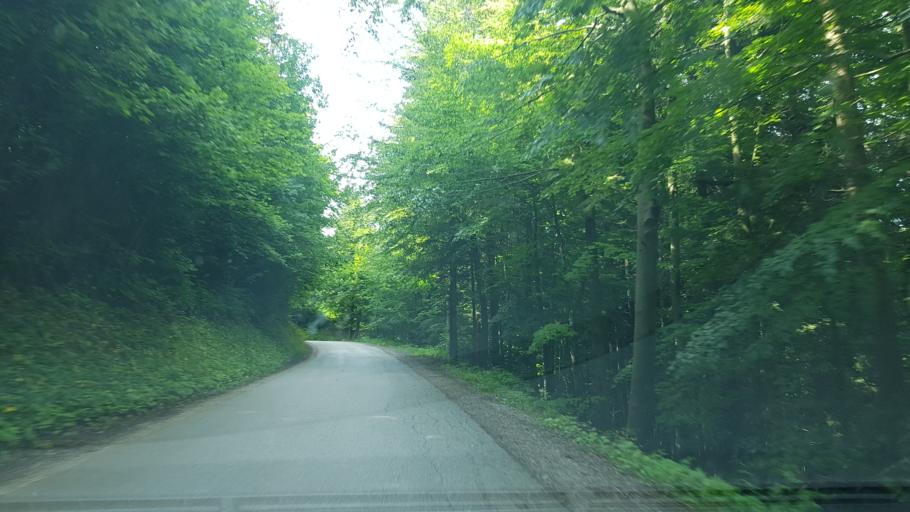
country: SI
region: Dobrna
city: Dobrna
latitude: 46.3837
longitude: 15.1836
